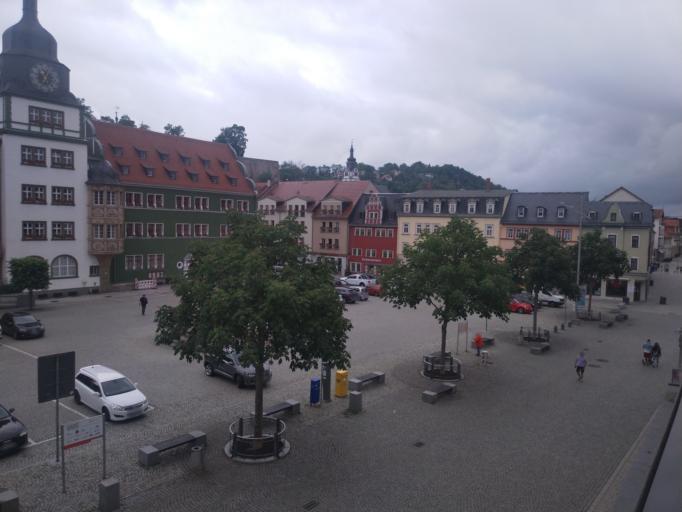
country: DE
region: Thuringia
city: Rudolstadt
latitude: 50.7204
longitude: 11.3396
